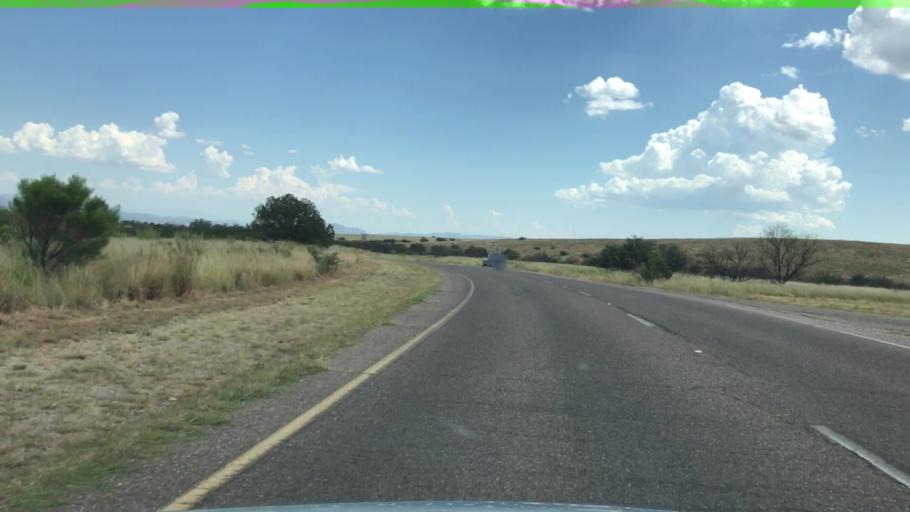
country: US
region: Arizona
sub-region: Cochise County
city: Sierra Vista
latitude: 31.5431
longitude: -110.3340
